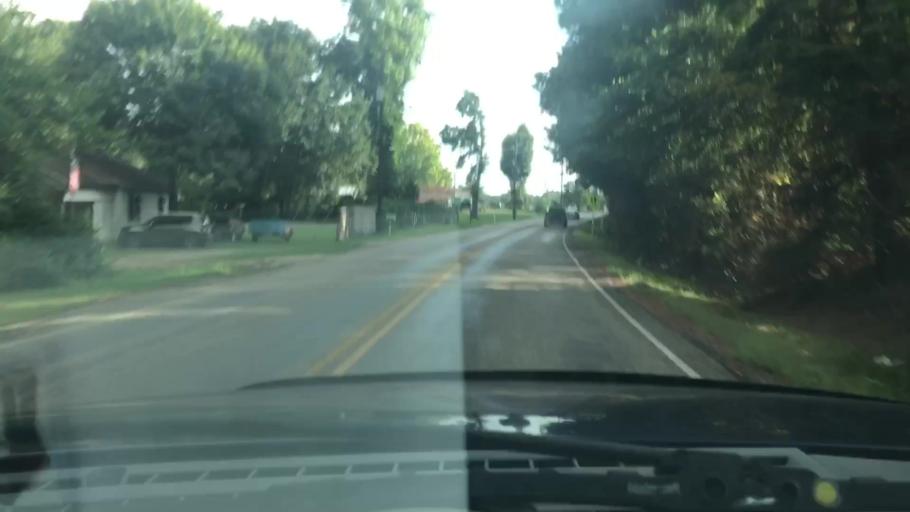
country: US
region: Texas
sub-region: Bowie County
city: Texarkana
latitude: 33.3986
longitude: -94.0639
